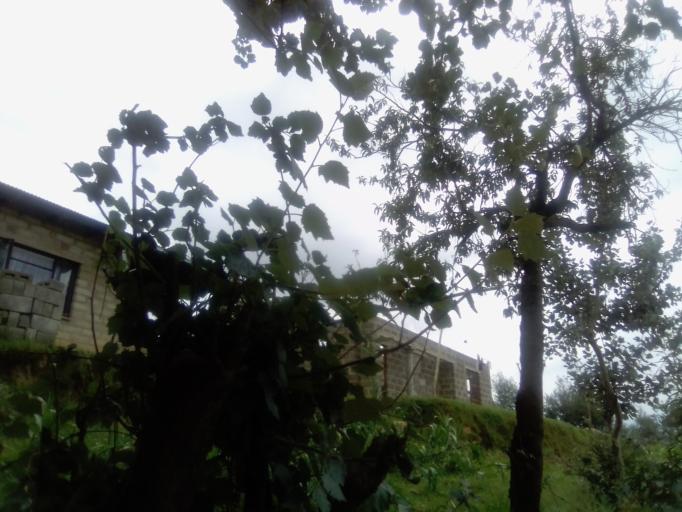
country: LS
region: Leribe
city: Leribe
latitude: -29.0363
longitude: 28.0209
